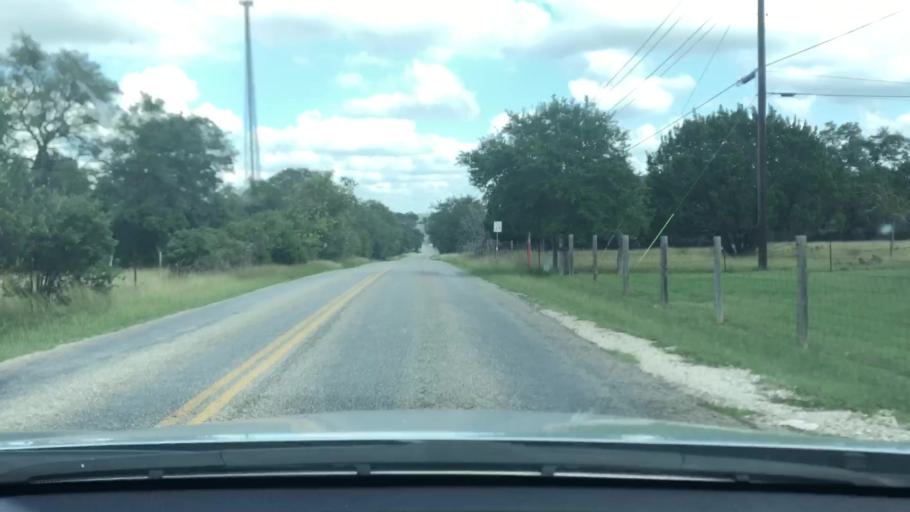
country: US
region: Texas
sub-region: Bexar County
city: Fair Oaks Ranch
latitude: 29.7853
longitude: -98.6372
